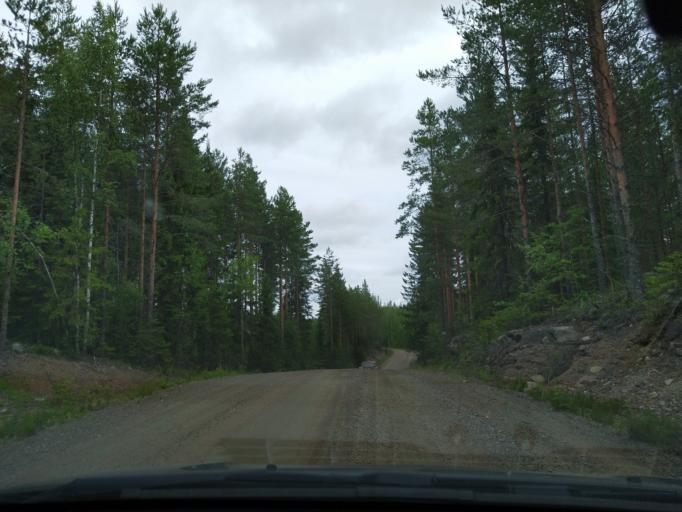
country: FI
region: Southern Savonia
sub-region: Mikkeli
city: Maentyharju
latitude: 61.1481
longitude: 26.8962
